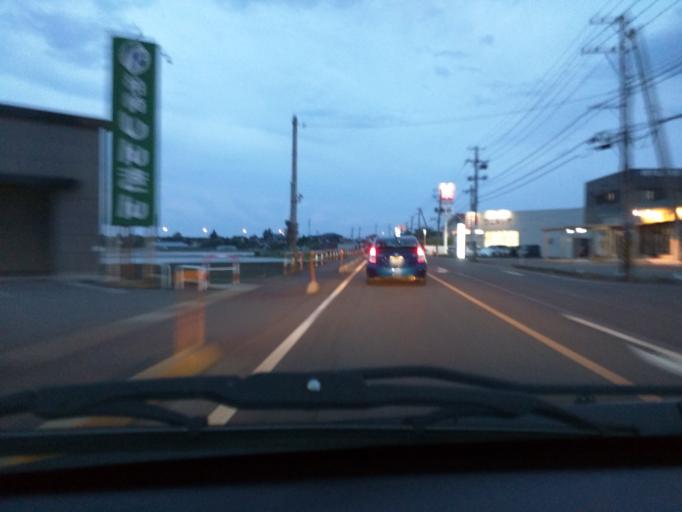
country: JP
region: Niigata
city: Kashiwazaki
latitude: 37.3558
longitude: 138.5970
